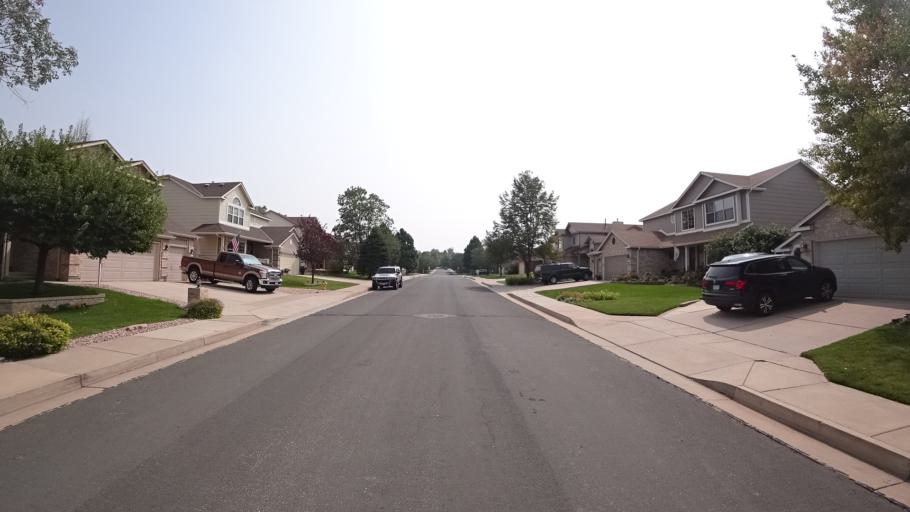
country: US
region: Colorado
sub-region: El Paso County
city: Cimarron Hills
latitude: 38.9189
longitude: -104.7476
